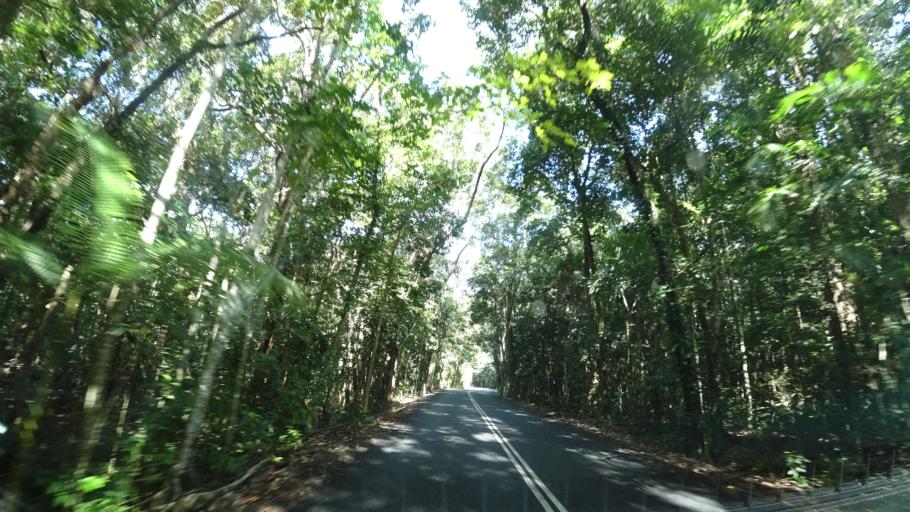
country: AU
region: Queensland
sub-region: Cairns
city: Port Douglas
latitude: -16.1368
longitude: 145.4507
